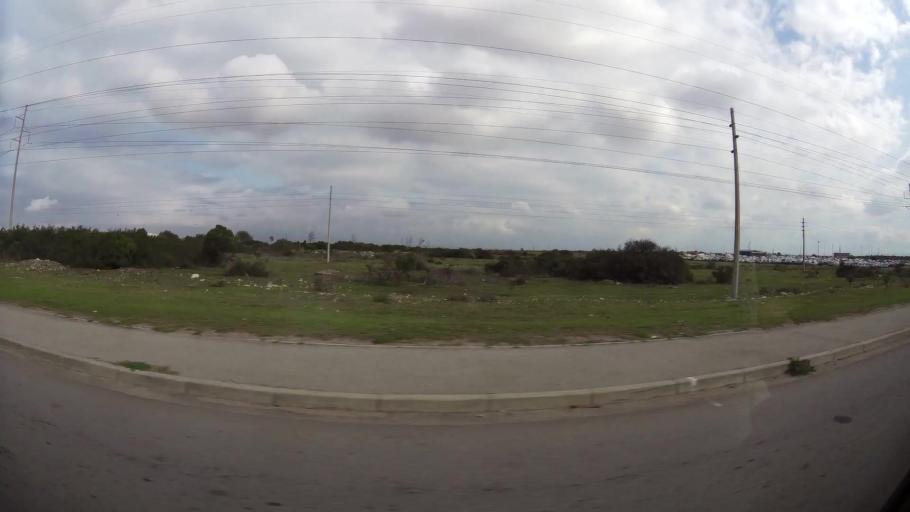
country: ZA
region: Eastern Cape
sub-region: Nelson Mandela Bay Metropolitan Municipality
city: Port Elizabeth
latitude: -33.8070
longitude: 25.6246
